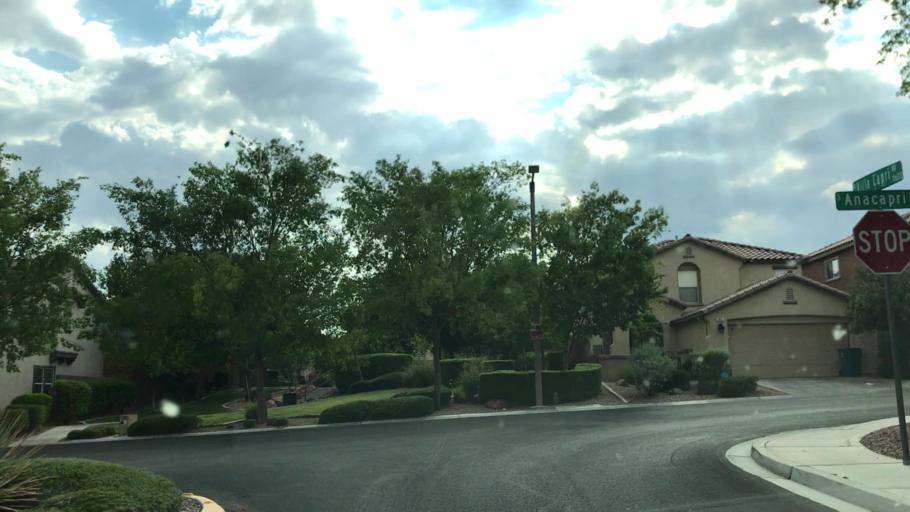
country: US
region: Nevada
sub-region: Clark County
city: Summerlin South
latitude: 36.1664
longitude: -115.3504
